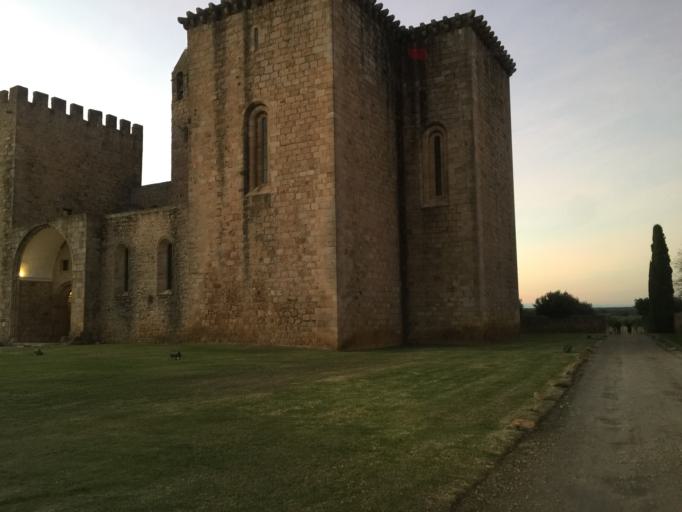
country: PT
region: Portalegre
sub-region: Alter do Chao
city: Alter do Chao
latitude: 39.3064
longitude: -7.6477
